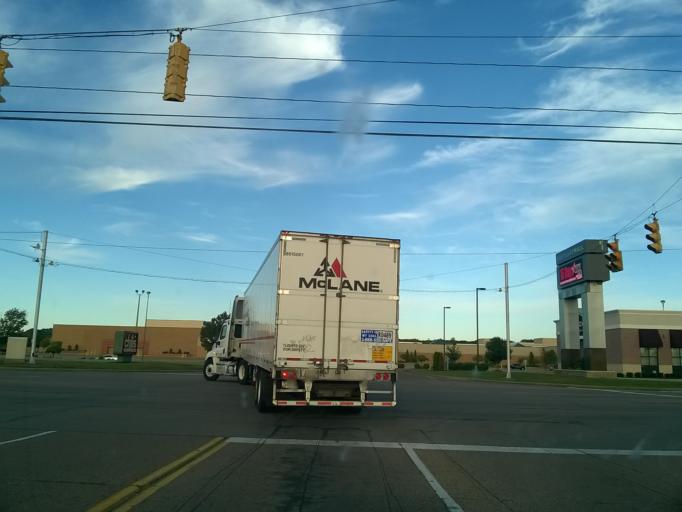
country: US
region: Indiana
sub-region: Vanderburgh County
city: Melody Hill
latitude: 37.9834
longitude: -87.4926
